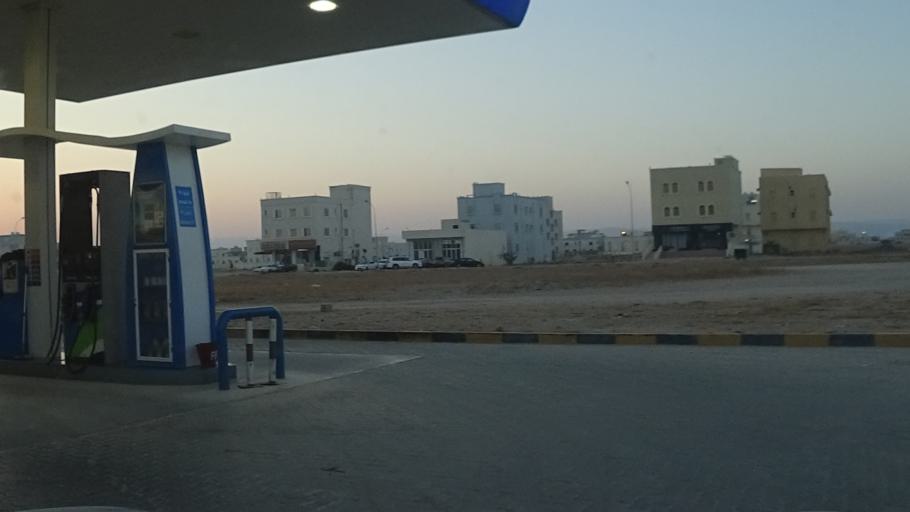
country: OM
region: Zufar
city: Salalah
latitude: 17.0485
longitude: 54.2118
